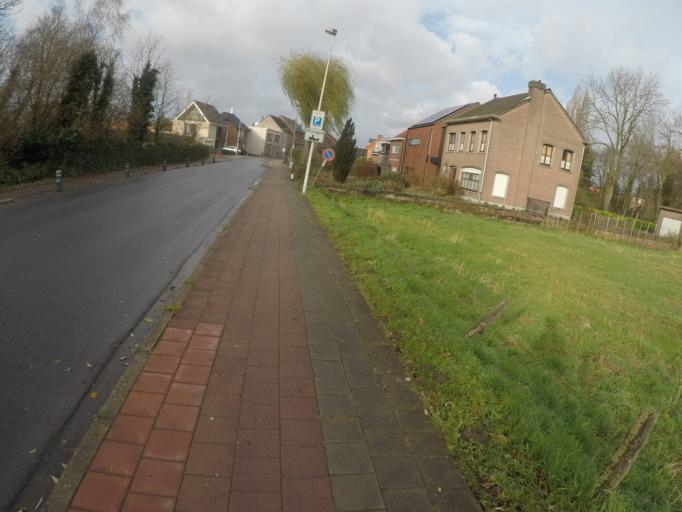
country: BE
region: Flanders
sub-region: Provincie Antwerpen
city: Wijnegem
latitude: 51.2235
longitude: 4.5228
